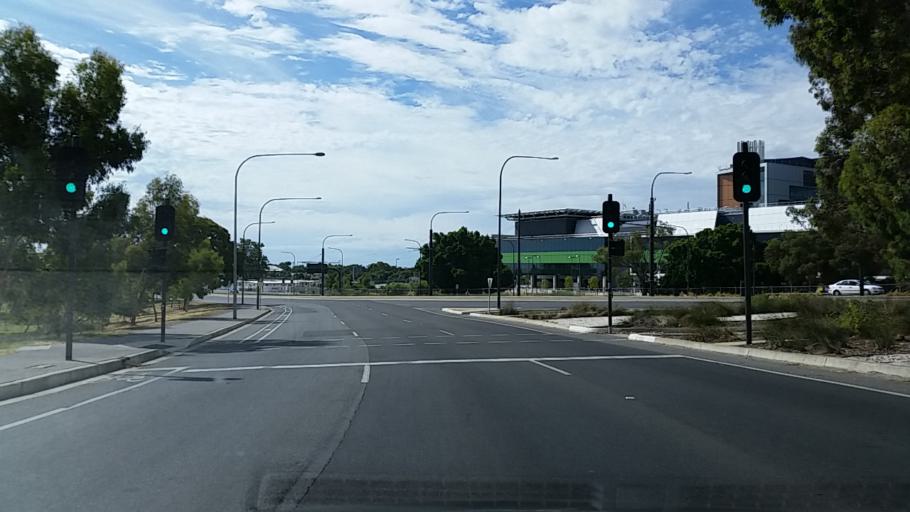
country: AU
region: South Australia
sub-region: Adelaide
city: Adelaide
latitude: -34.9226
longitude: 138.5871
